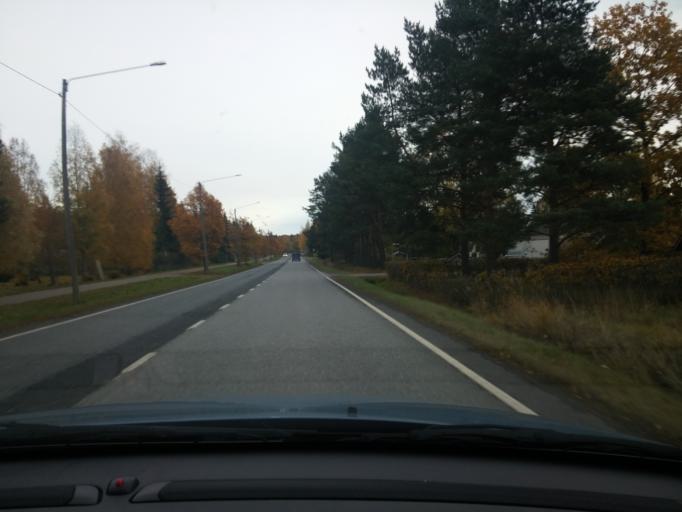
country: FI
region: Haeme
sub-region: Forssa
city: Tammela
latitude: 60.8070
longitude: 23.7857
